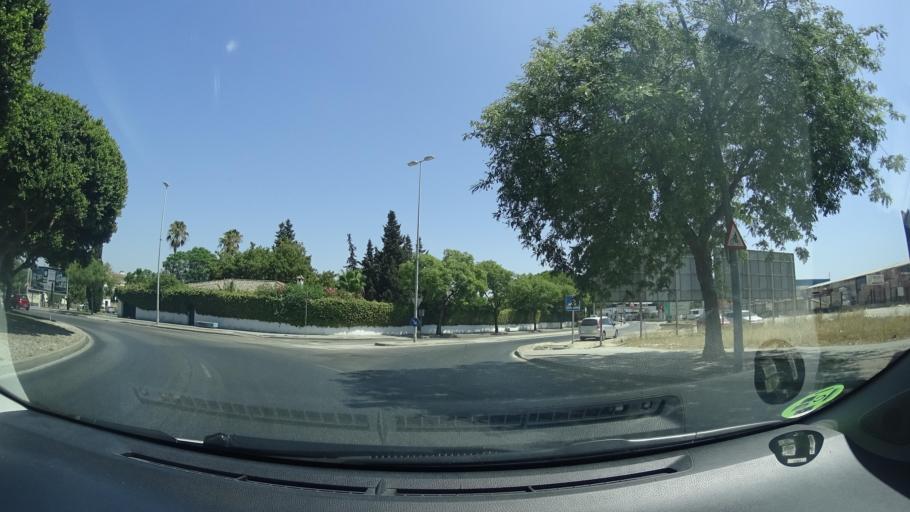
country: ES
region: Andalusia
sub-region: Provincia de Cadiz
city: Jerez de la Frontera
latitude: 36.6729
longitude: -6.1224
